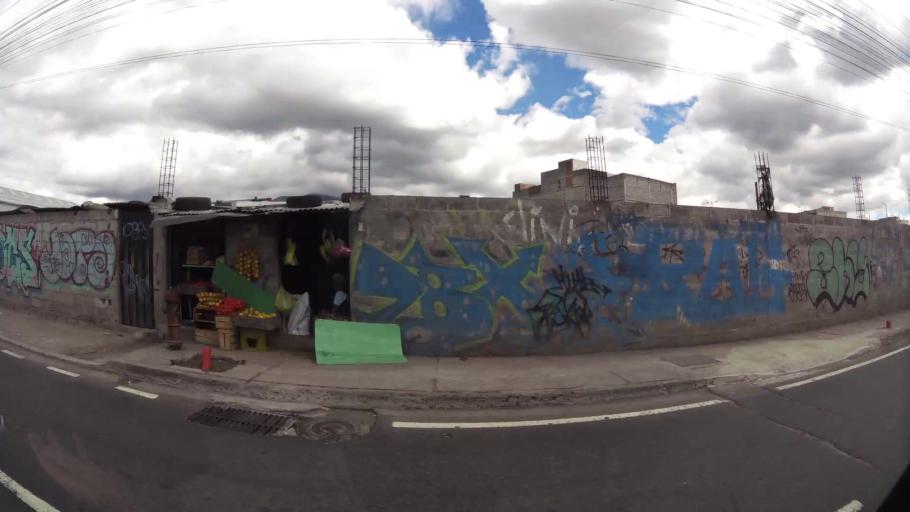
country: EC
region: Pichincha
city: Sangolqui
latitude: -0.3319
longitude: -78.5506
